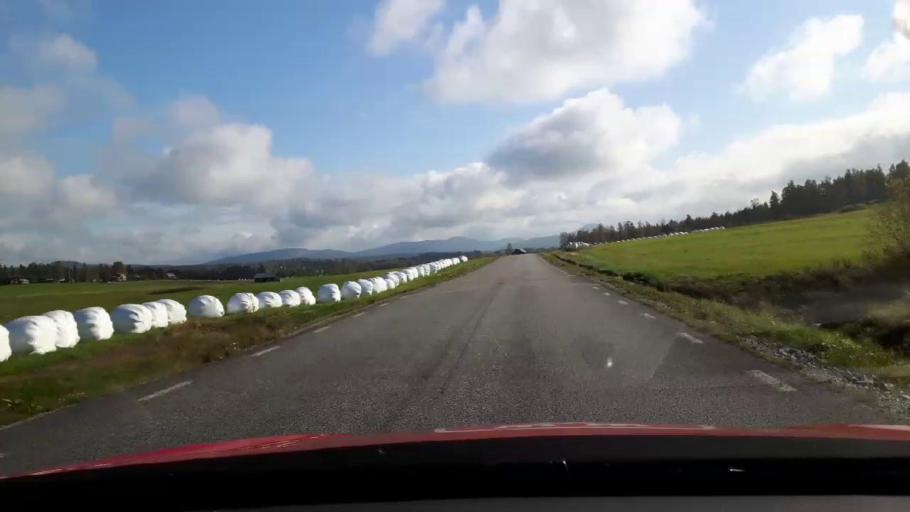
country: SE
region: Gaevleborg
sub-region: Ljusdals Kommun
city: Ljusdal
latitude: 61.7629
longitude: 16.0699
